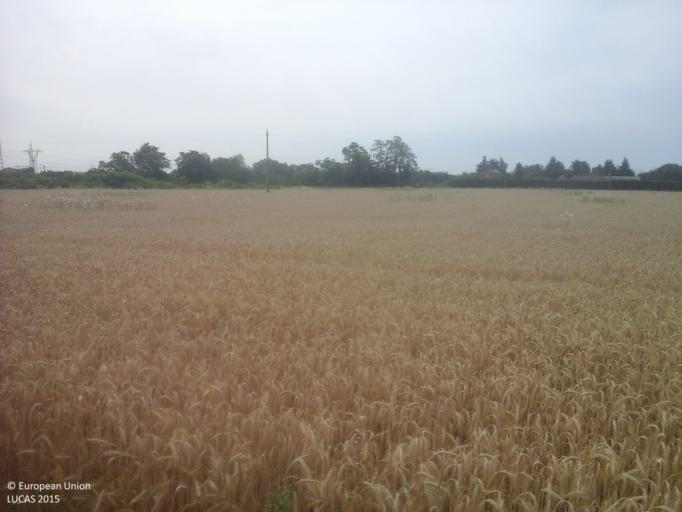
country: IT
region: Lombardy
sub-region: Provincia di Monza e Brianza
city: Concorezzo
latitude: 45.5932
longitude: 9.3478
